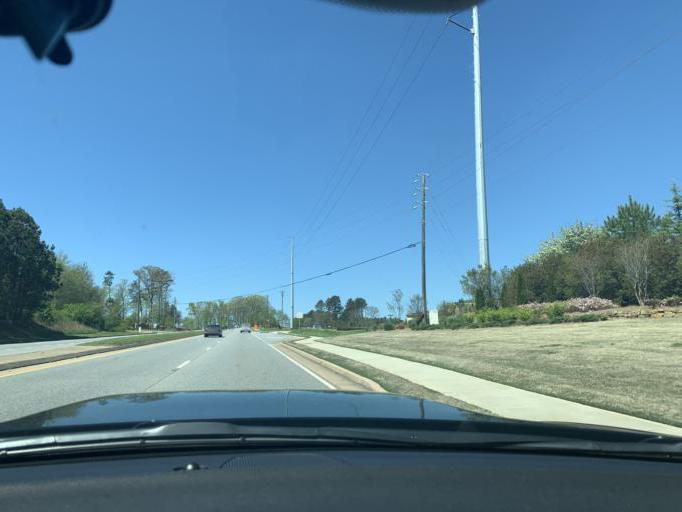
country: US
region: Georgia
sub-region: Forsyth County
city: Cumming
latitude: 34.1553
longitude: -84.1633
